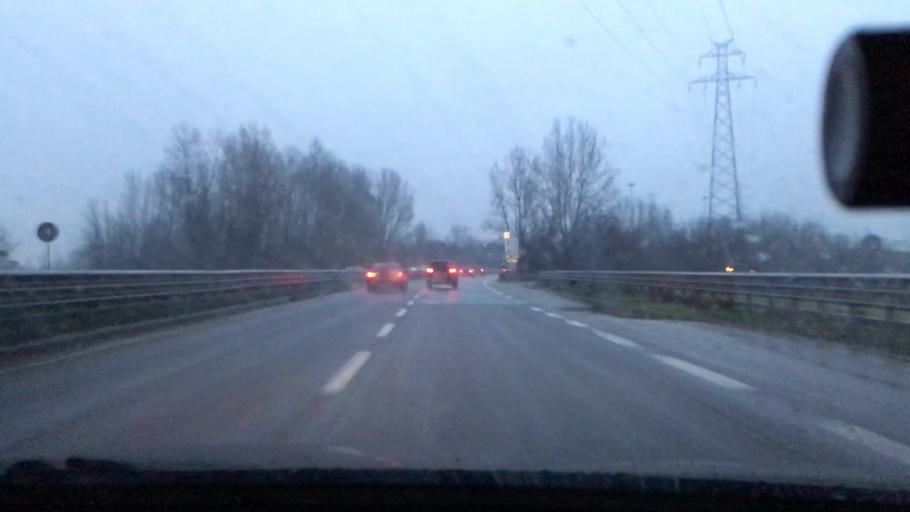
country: IT
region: Emilia-Romagna
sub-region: Provincia di Modena
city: Baggiovara
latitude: 44.6404
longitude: 10.8788
